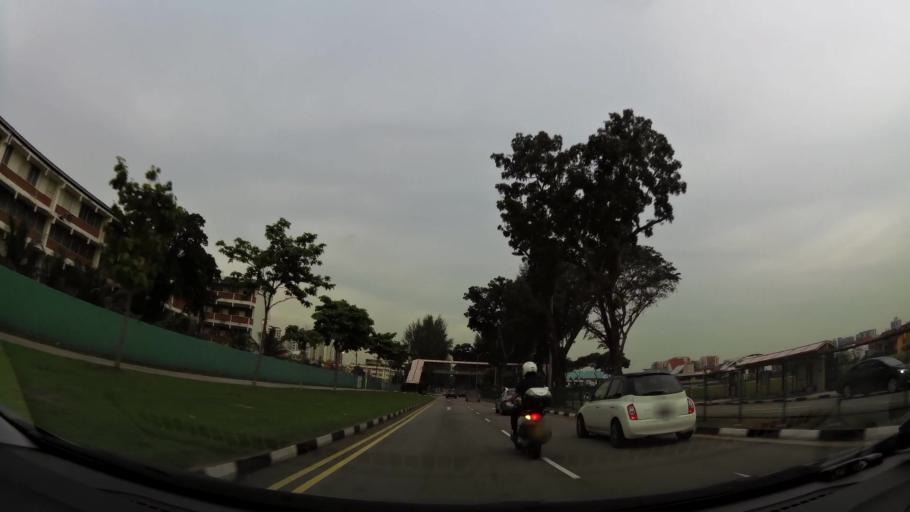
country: SG
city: Singapore
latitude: 1.3088
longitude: 103.8904
